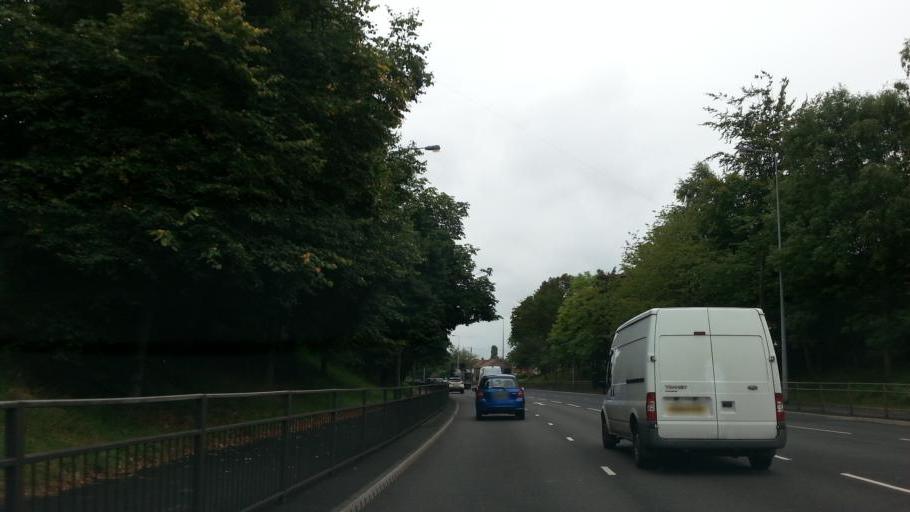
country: GB
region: England
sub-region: Borough of Oldham
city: Oldham
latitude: 53.5437
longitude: -2.1480
